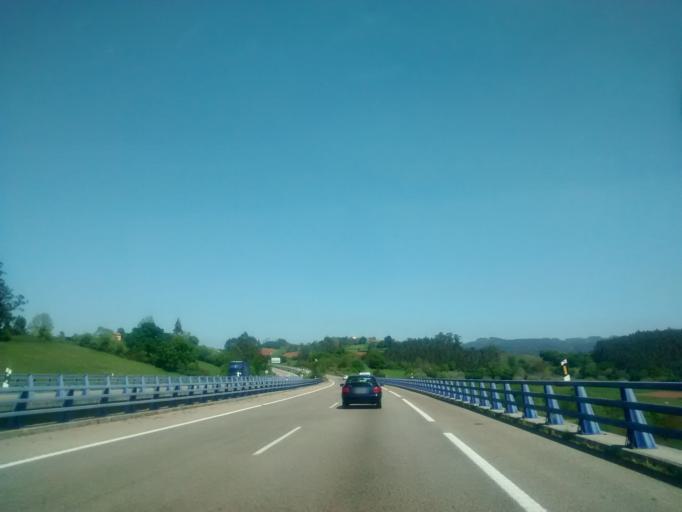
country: ES
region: Asturias
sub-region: Province of Asturias
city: Villaviciosa
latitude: 43.4701
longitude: -5.4721
